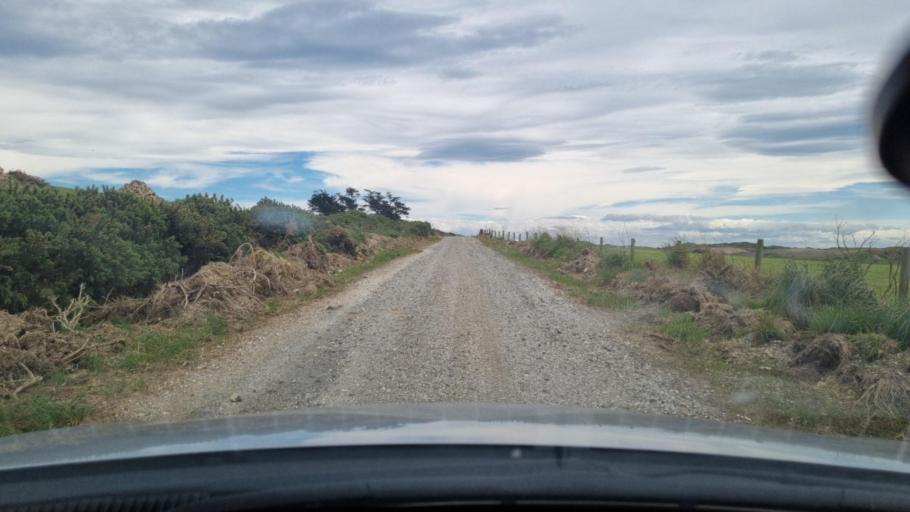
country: NZ
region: Southland
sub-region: Invercargill City
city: Bluff
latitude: -46.5202
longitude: 168.2964
